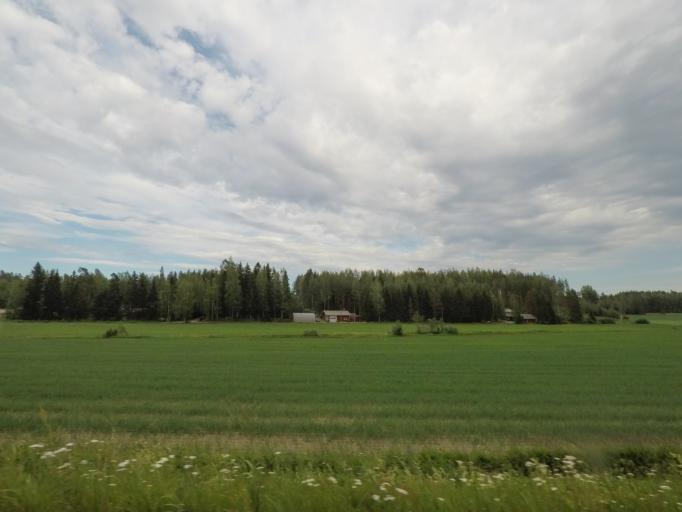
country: FI
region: Uusimaa
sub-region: Porvoo
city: Pukkila
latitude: 60.7706
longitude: 25.4501
